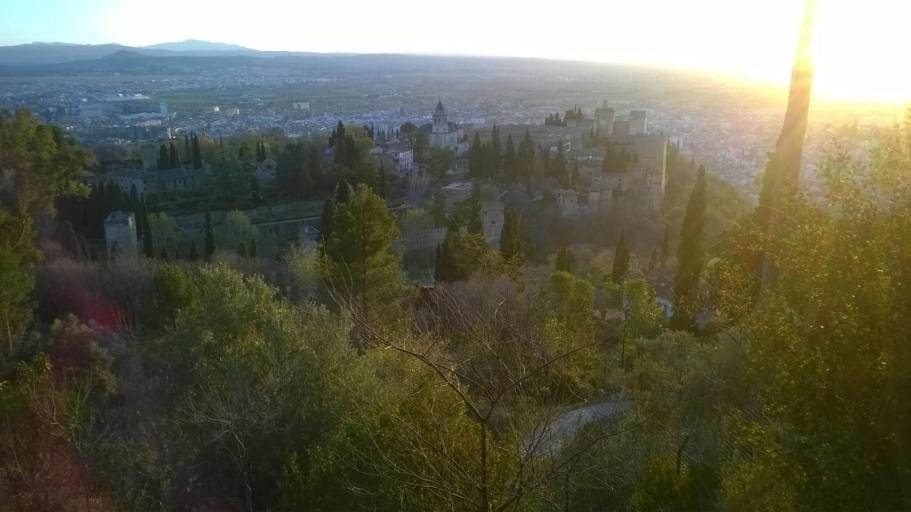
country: ES
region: Andalusia
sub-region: Provincia de Granada
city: Granada
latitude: 37.1777
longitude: -3.5839
